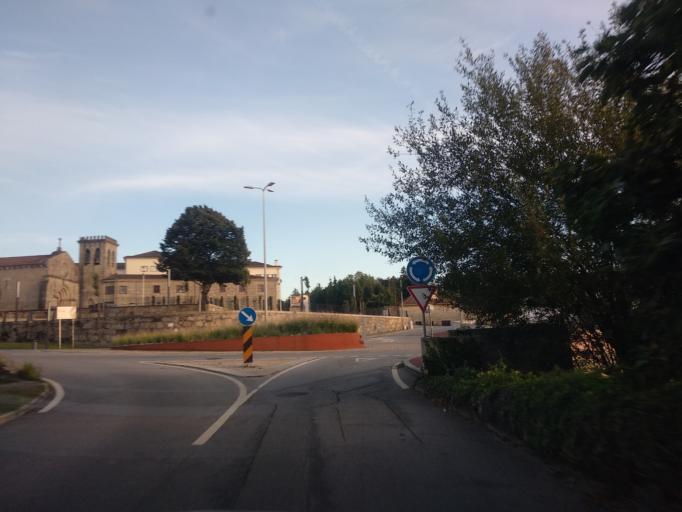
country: PT
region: Braga
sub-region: Vila Nova de Famalicao
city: Vila Nova de Famalicao
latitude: 41.4032
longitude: -8.5104
